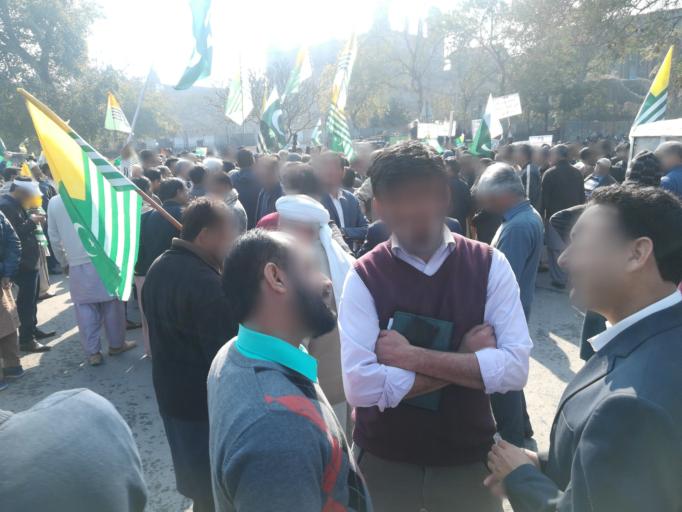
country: PK
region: Punjab
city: Lahore
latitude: 31.5688
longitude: 74.3068
